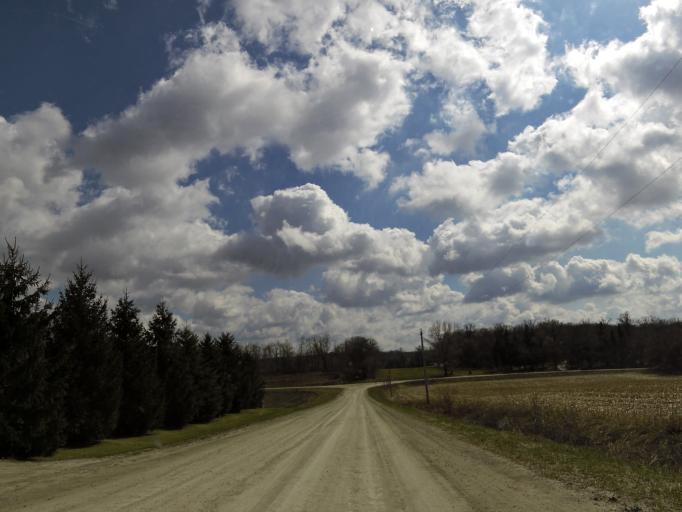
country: US
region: Minnesota
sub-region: Dodge County
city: Mantorville
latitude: 44.0698
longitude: -92.7182
